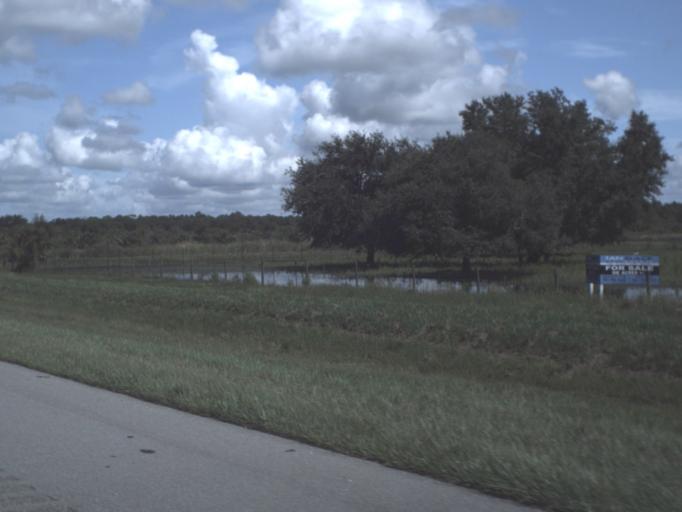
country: US
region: Florida
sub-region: Sarasota County
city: Laurel
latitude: 27.1603
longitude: -82.4268
